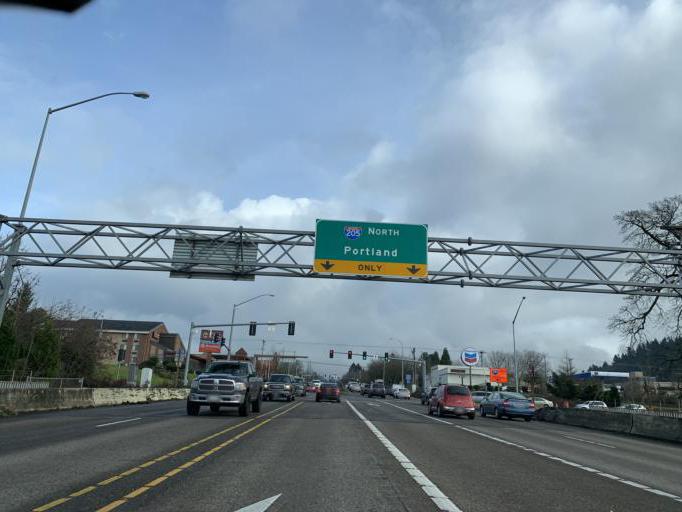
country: US
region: Oregon
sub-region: Clackamas County
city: Clackamas
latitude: 45.4333
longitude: -122.5657
